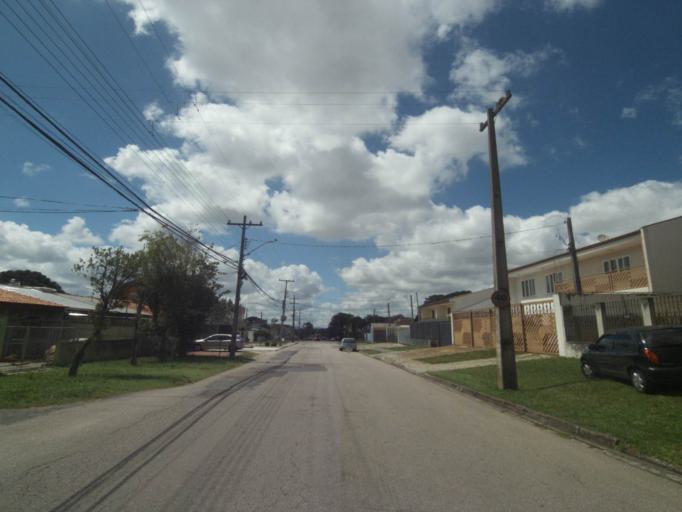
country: BR
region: Parana
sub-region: Pinhais
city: Pinhais
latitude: -25.4384
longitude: -49.2168
